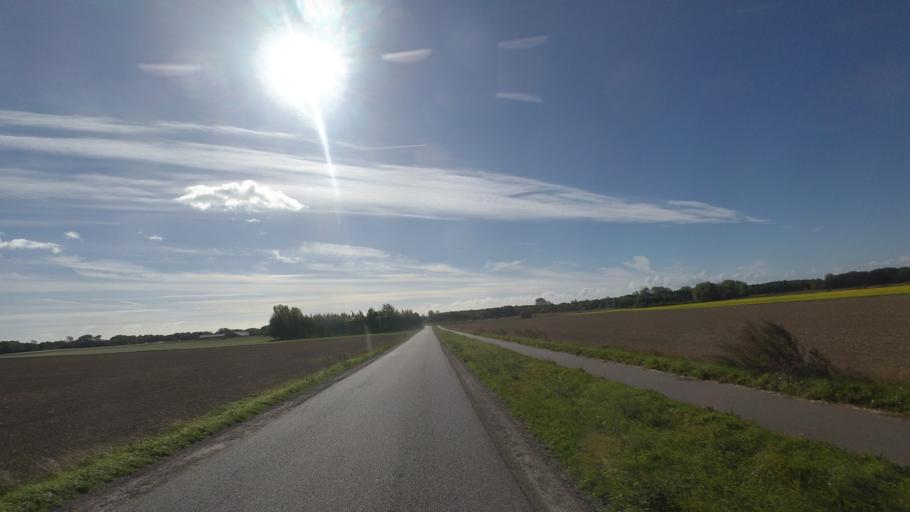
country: DK
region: Capital Region
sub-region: Bornholm Kommune
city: Akirkeby
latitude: 55.0166
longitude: 14.9921
